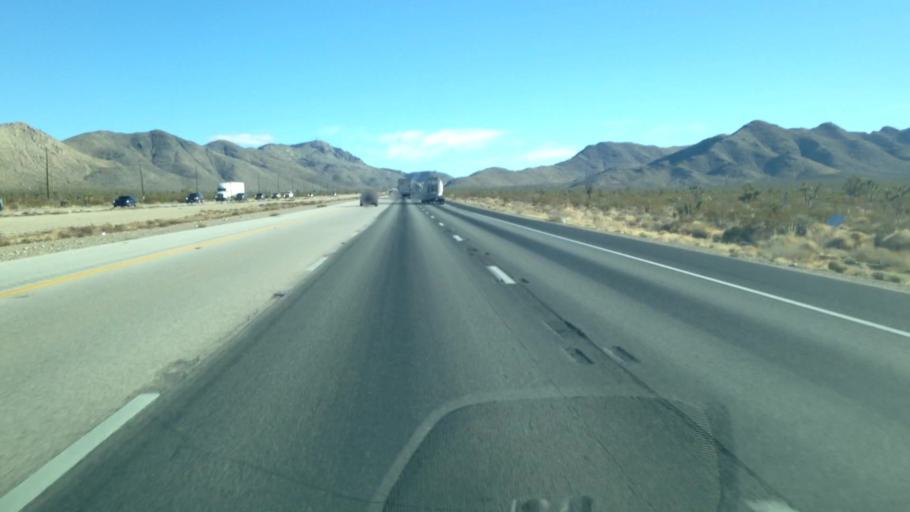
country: US
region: Nevada
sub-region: Clark County
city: Sandy Valley
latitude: 35.4608
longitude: -115.6261
